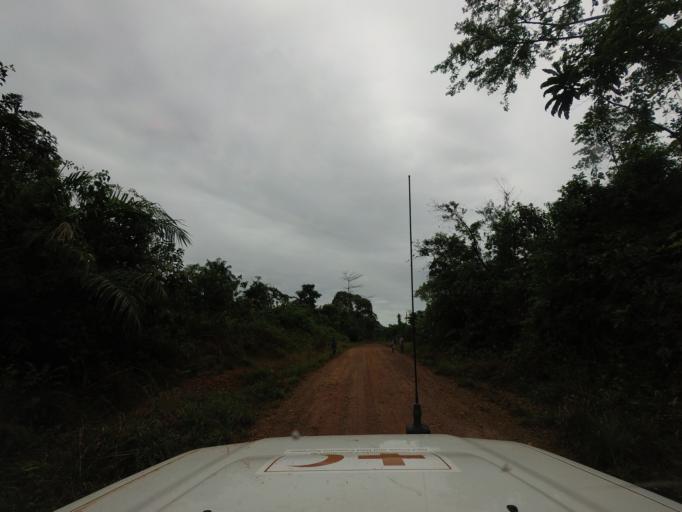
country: LR
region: Nimba
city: New Yekepa
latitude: 7.5792
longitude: -8.5603
